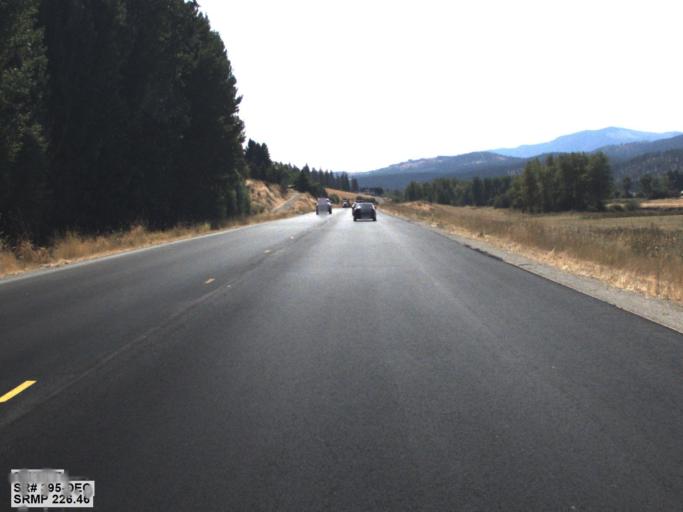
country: US
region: Washington
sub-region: Stevens County
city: Colville
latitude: 48.5012
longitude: -117.9022
